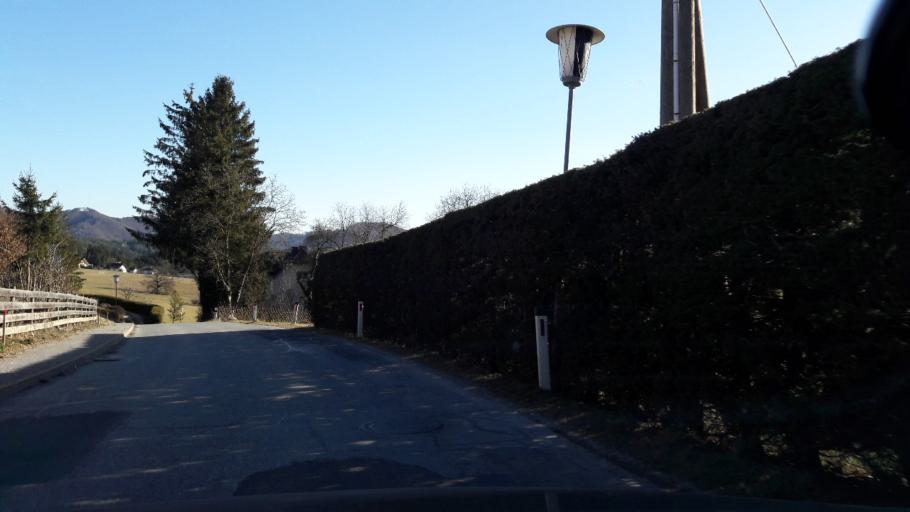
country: AT
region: Styria
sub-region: Politischer Bezirk Graz-Umgebung
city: Eisbach
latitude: 47.1304
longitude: 15.2873
